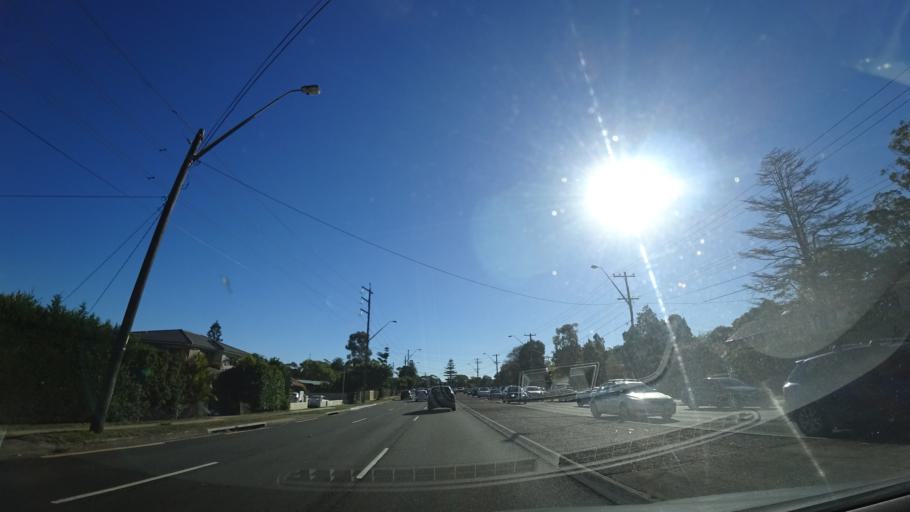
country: AU
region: New South Wales
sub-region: Warringah
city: Forestville
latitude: -33.7548
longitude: 151.2225
